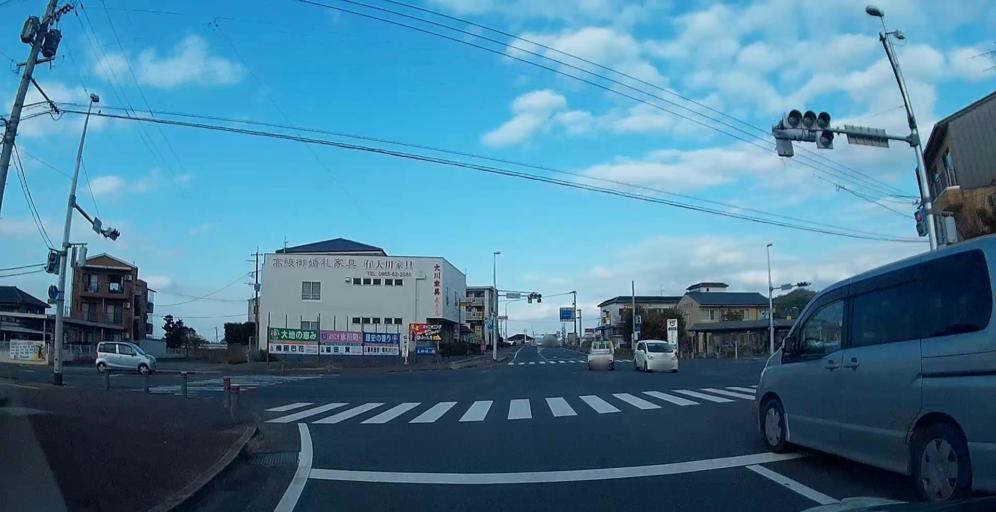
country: JP
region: Kumamoto
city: Matsubase
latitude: 32.5572
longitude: 130.6815
